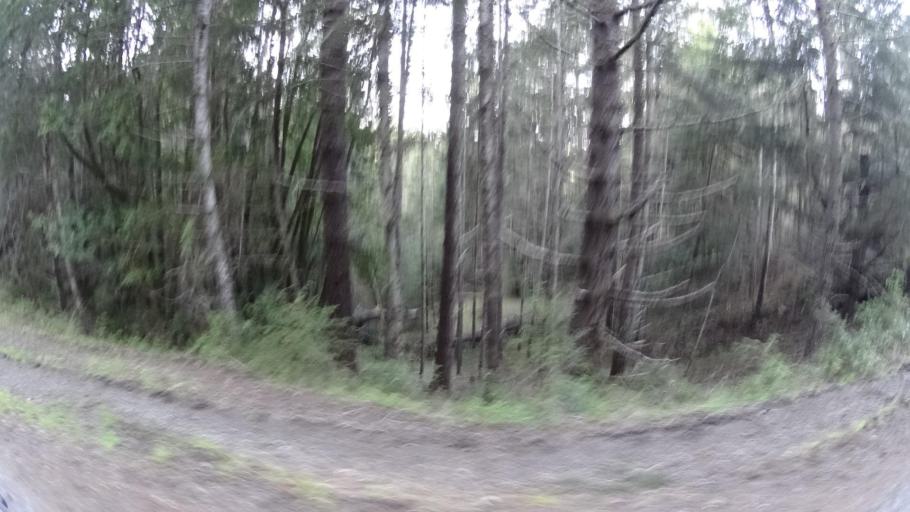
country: US
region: California
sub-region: Humboldt County
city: Bayside
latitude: 40.6847
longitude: -123.9370
